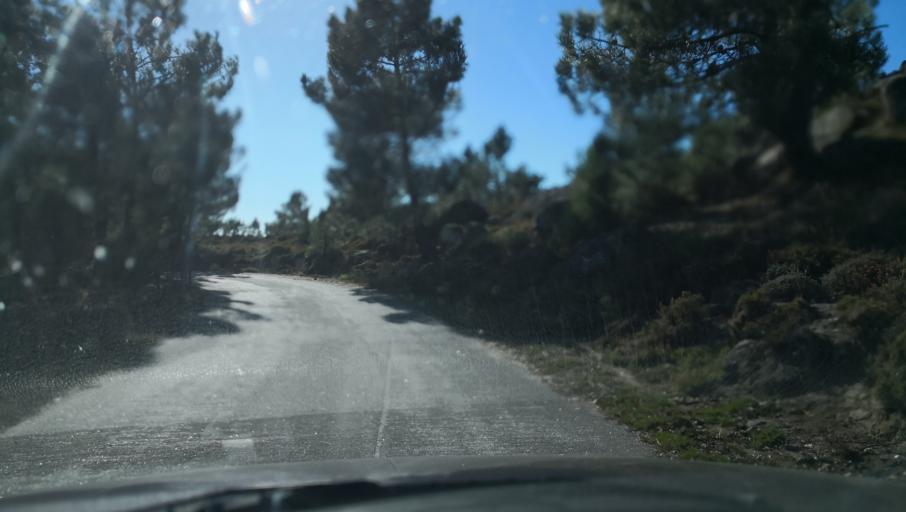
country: PT
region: Vila Real
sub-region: Vila Real
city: Vila Real
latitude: 41.3311
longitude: -7.7866
